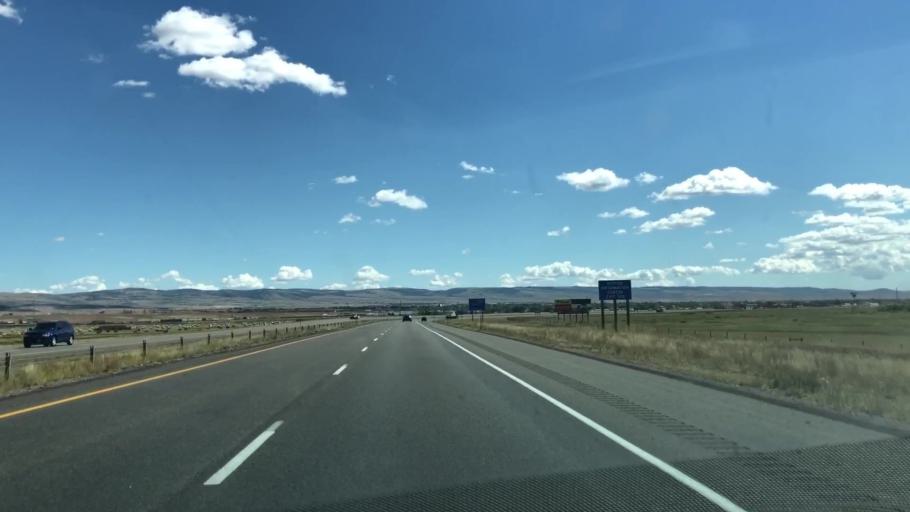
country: US
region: Wyoming
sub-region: Albany County
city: Laramie
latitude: 41.3424
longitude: -105.6231
